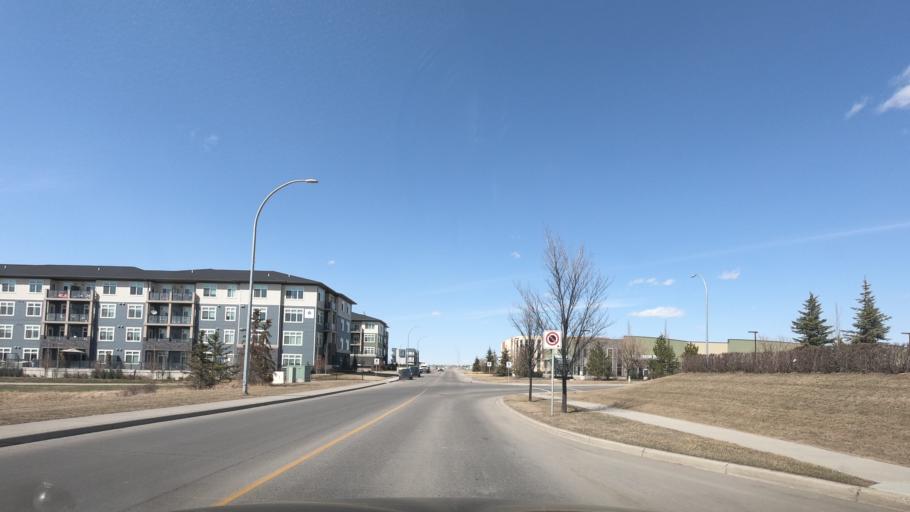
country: CA
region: Alberta
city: Airdrie
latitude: 51.3036
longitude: -114.0112
